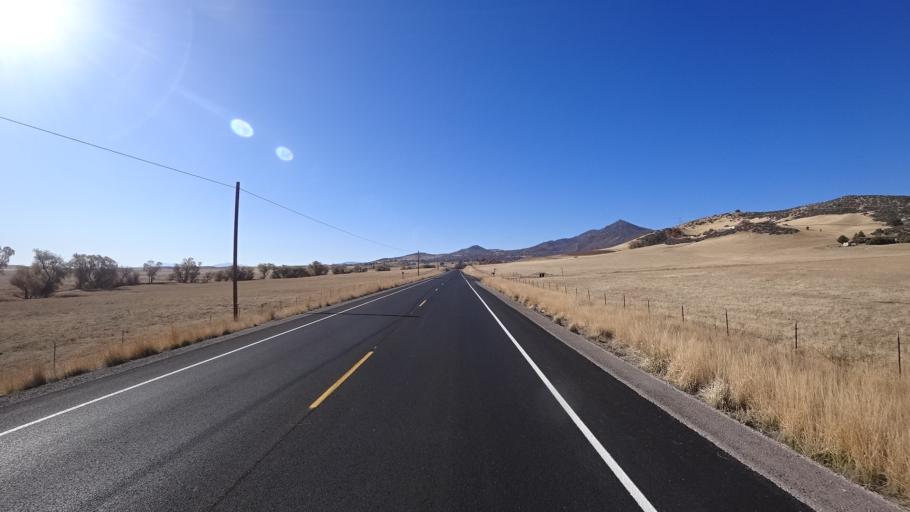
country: US
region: California
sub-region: Siskiyou County
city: Montague
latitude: 41.8335
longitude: -122.4874
